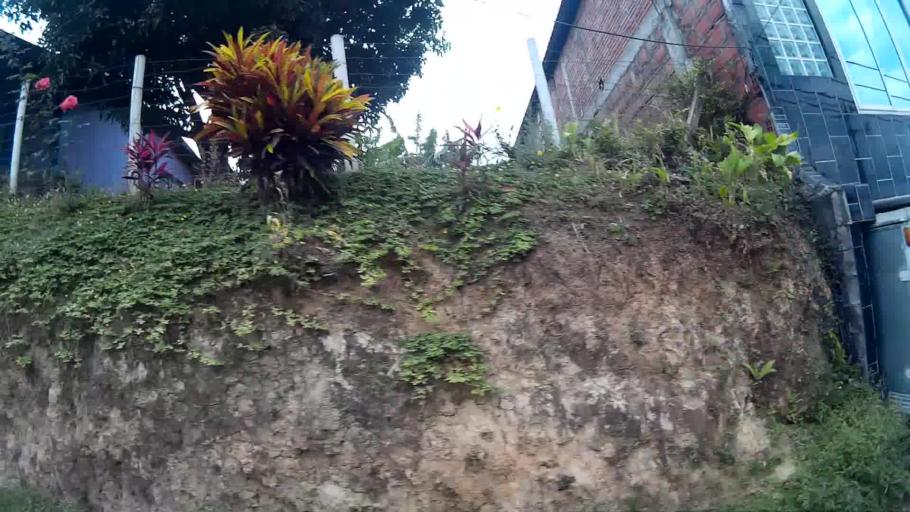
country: CO
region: Valle del Cauca
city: Ulloa
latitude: 4.7406
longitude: -75.7135
